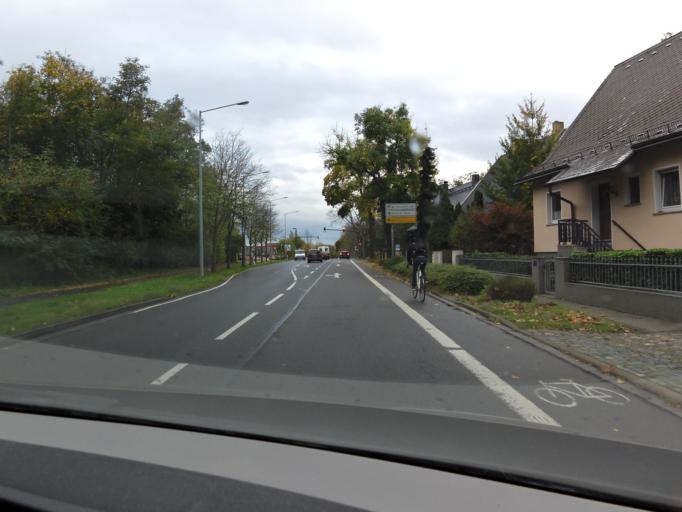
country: DE
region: Saxony
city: Markkleeberg
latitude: 51.2749
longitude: 12.3565
